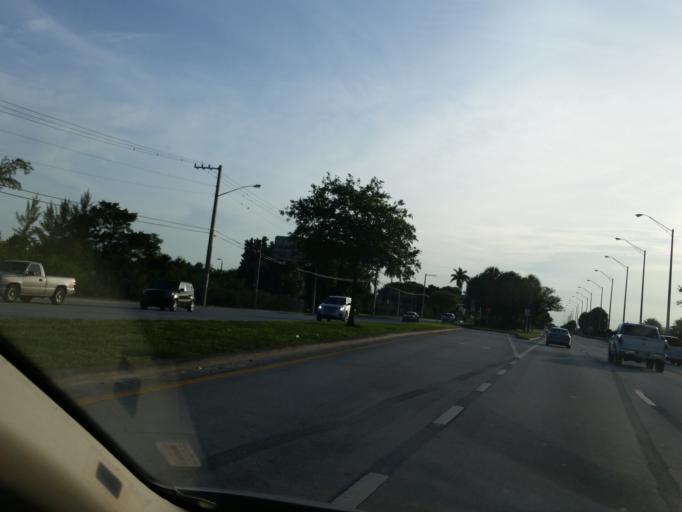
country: US
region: Florida
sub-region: Broward County
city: Davie
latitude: 26.0656
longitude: -80.2165
